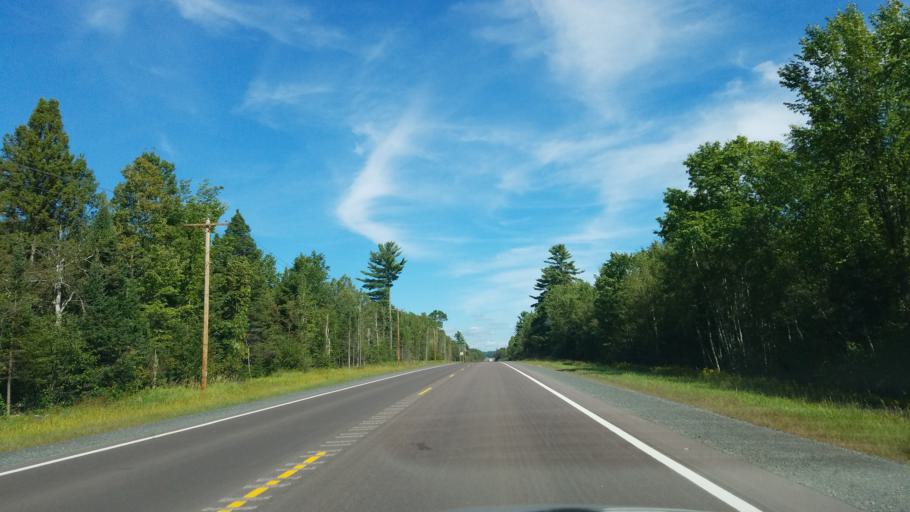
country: US
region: Michigan
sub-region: Iron County
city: Iron River
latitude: 46.4891
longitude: -88.8634
